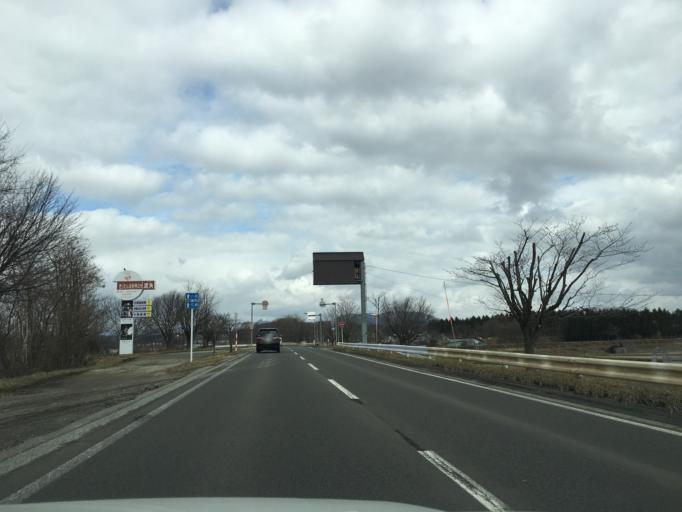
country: JP
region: Akita
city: Hanawa
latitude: 40.2587
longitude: 140.7628
